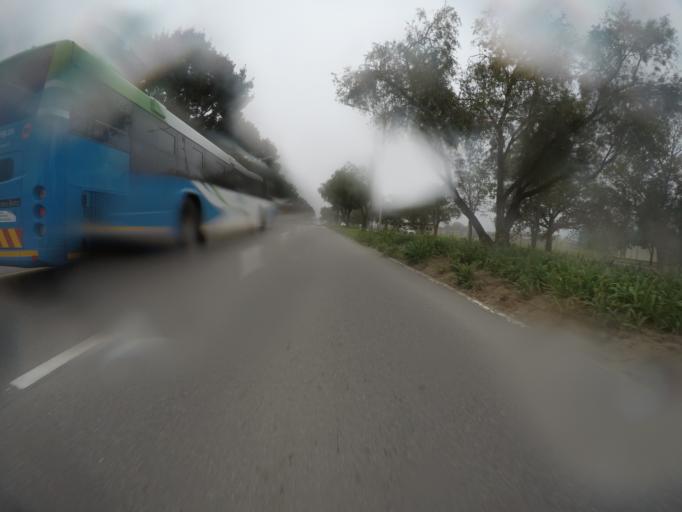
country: ZA
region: Western Cape
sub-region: Eden District Municipality
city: George
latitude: -33.9747
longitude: 22.4442
